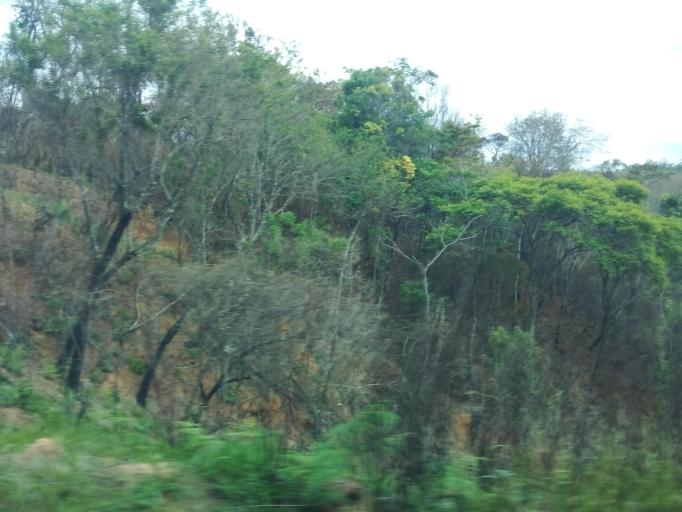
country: BR
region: Minas Gerais
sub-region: Caete
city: Caete
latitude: -19.9098
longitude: -43.6976
